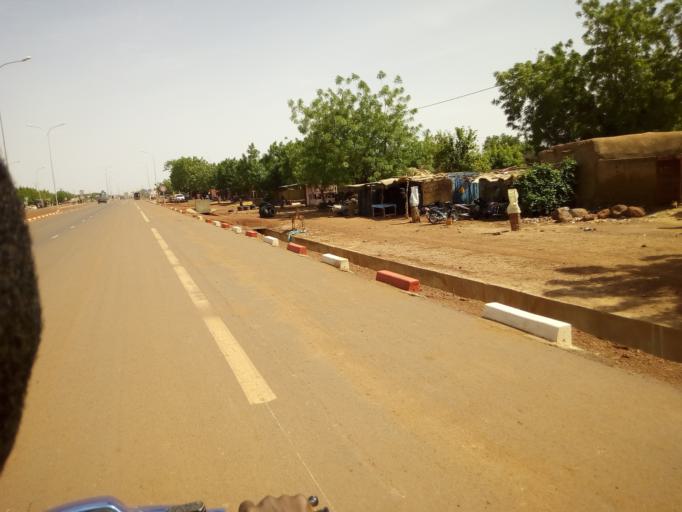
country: ML
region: Segou
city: Segou
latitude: 13.4240
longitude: -6.2167
